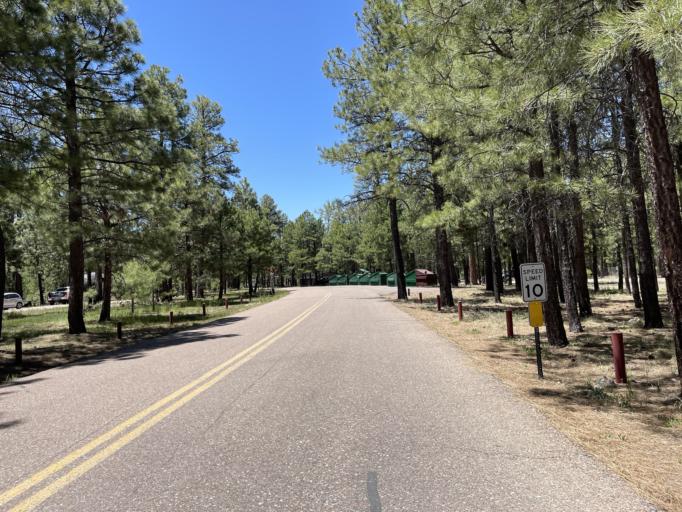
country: US
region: Arizona
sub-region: Navajo County
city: Heber-Overgaard
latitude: 34.3241
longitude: -110.8258
